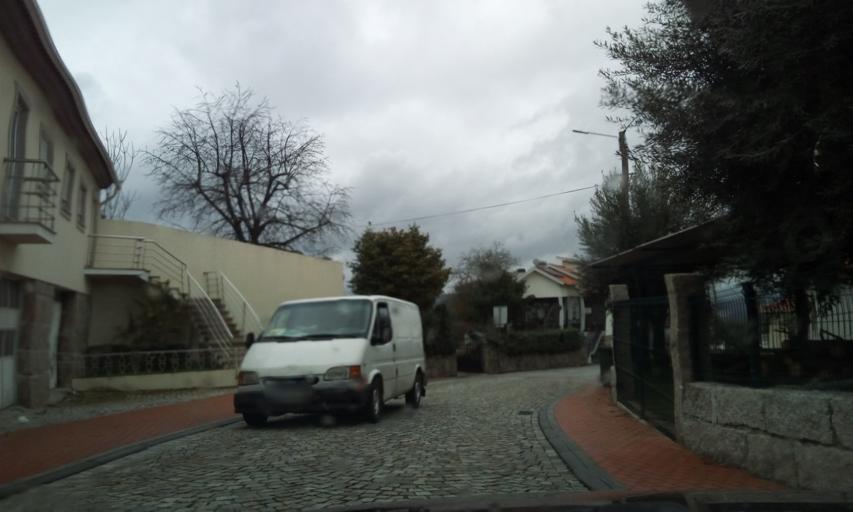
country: PT
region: Viseu
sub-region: Nelas
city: Nelas
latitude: 40.6014
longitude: -7.8454
